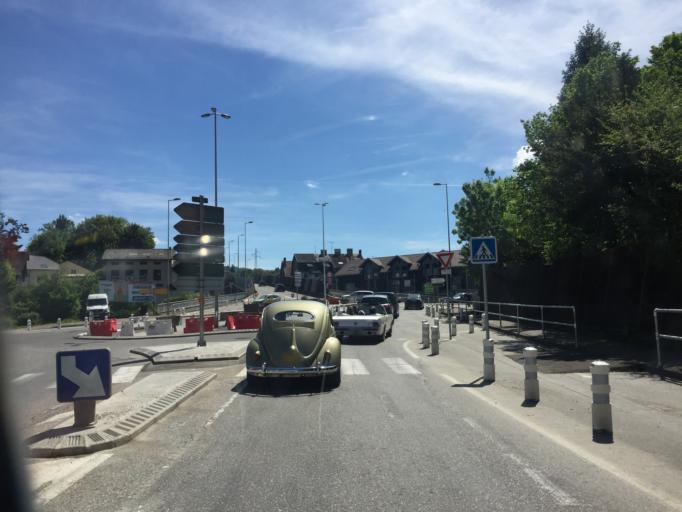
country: FR
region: Rhone-Alpes
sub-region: Departement de la Haute-Savoie
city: Rumilly
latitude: 45.8713
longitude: 5.9420
